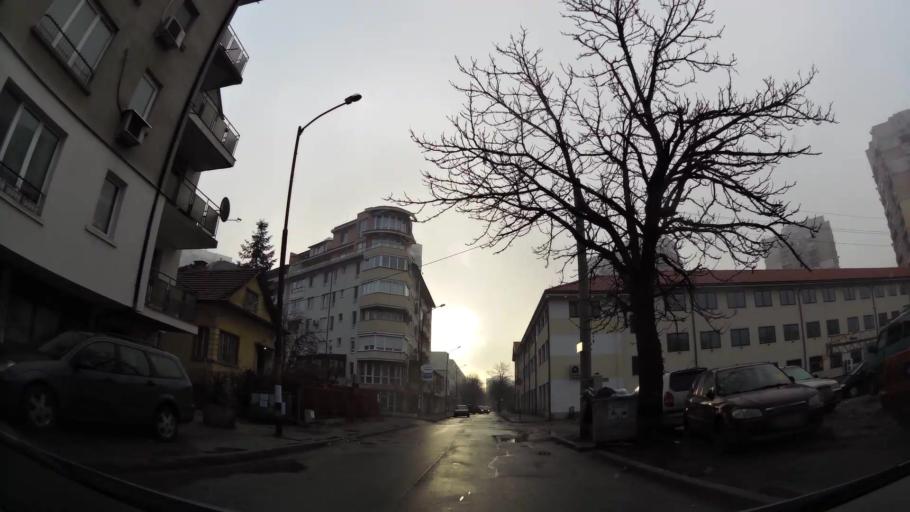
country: BG
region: Sofia-Capital
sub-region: Stolichna Obshtina
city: Sofia
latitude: 42.7309
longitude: 23.3038
